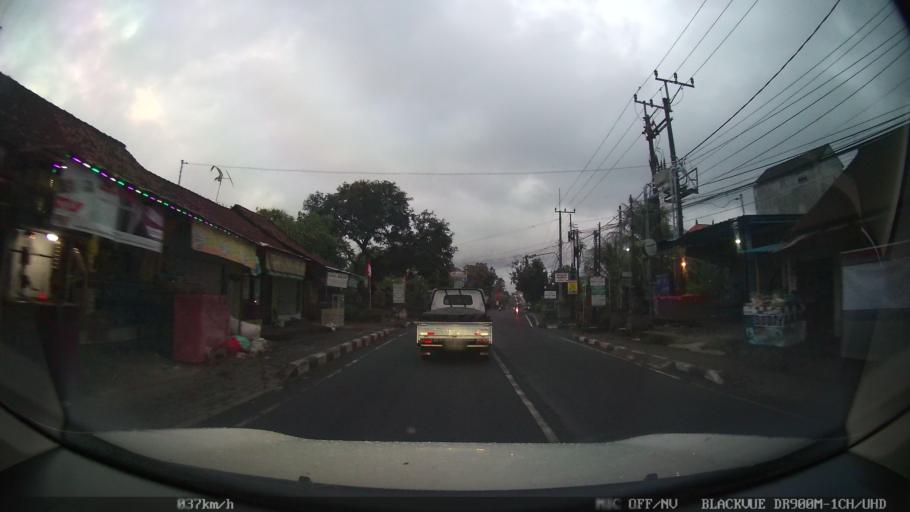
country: ID
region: Bali
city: Banjar Mambalkajanan
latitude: -8.5510
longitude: 115.2270
